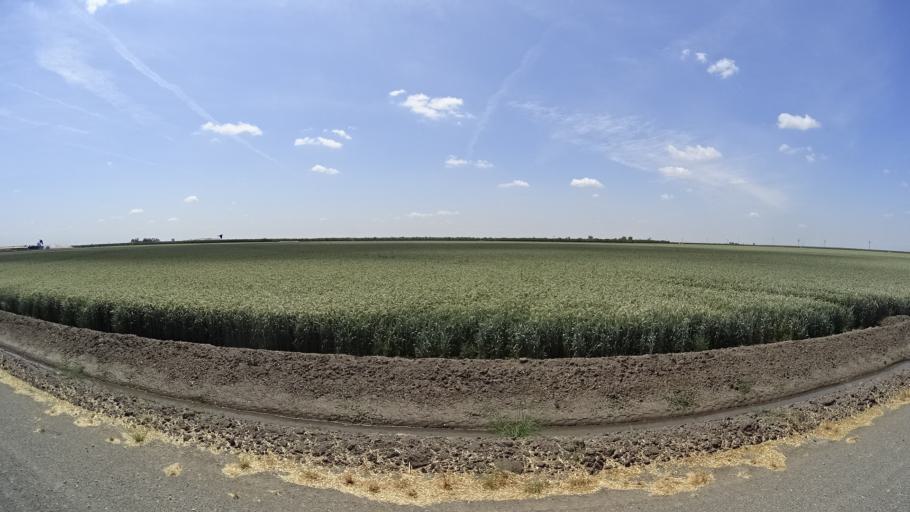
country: US
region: California
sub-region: Tulare County
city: Goshen
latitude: 36.2833
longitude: -119.4881
